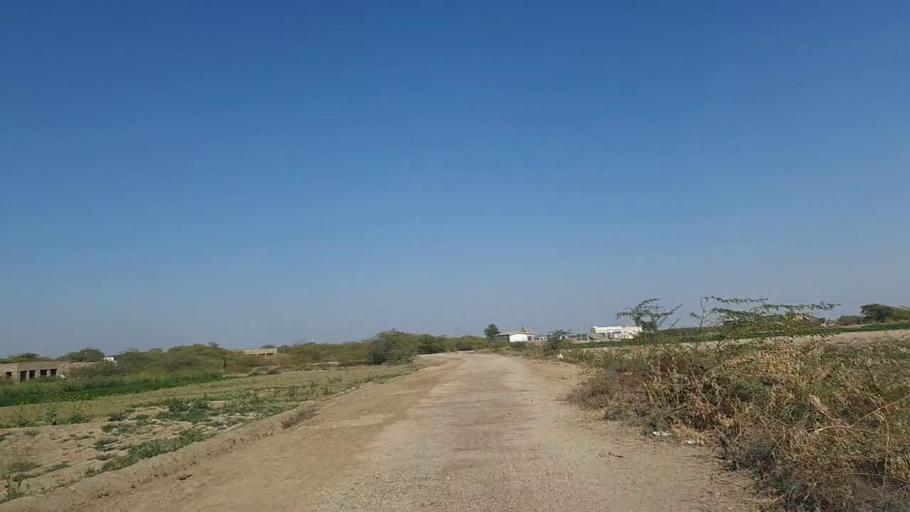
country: PK
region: Sindh
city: Naukot
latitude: 25.0229
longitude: 69.3600
